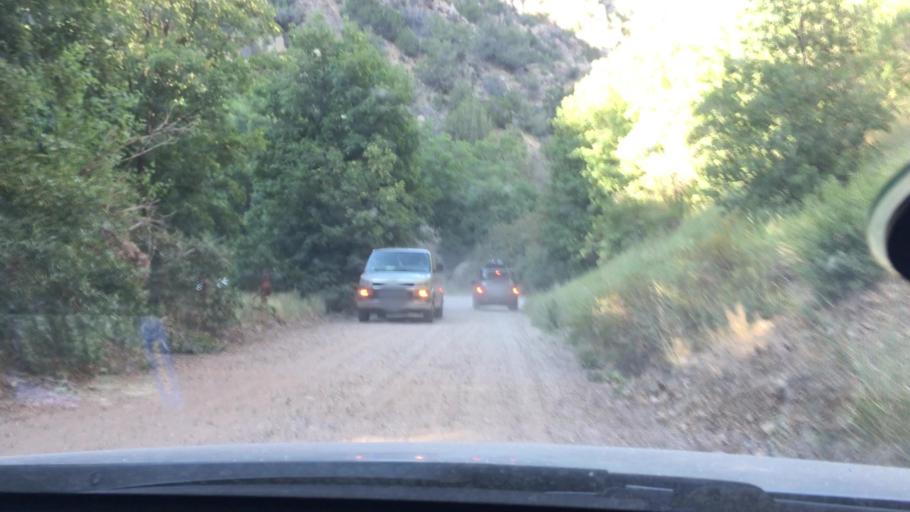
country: US
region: Utah
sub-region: Sanpete County
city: Fountain Green
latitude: 39.5550
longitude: -111.6706
